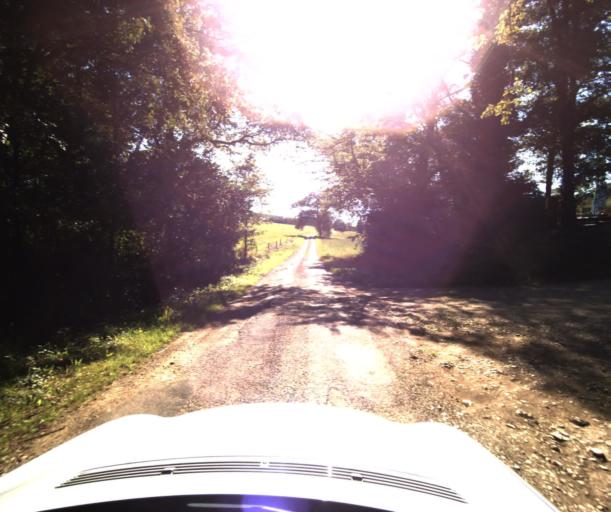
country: FR
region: Midi-Pyrenees
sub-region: Departement de l'Ariege
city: Lavelanet
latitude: 42.9720
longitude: 1.8987
